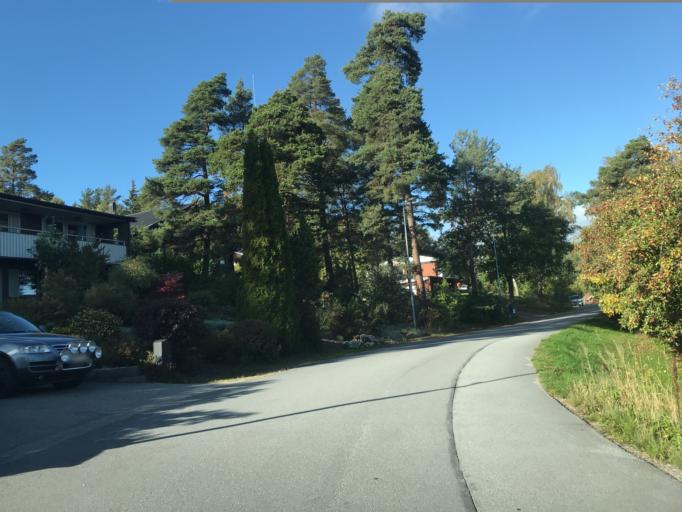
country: SE
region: Stockholm
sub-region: Sollentuna Kommun
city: Sollentuna
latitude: 59.4303
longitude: 17.9306
